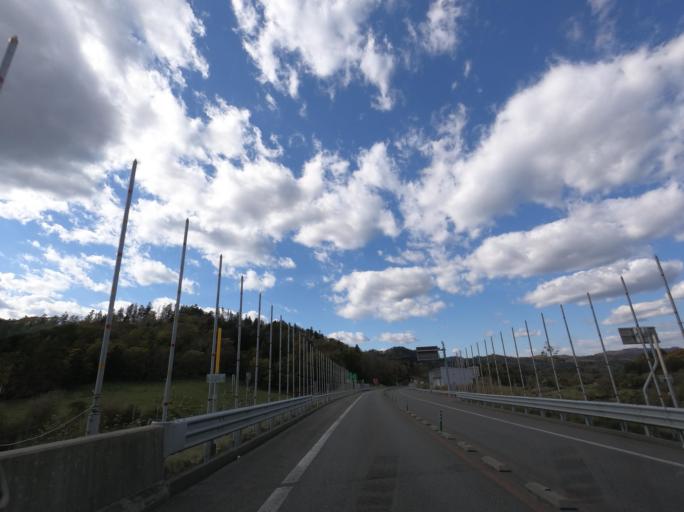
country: JP
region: Hokkaido
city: Kushiro
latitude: 43.0755
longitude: 144.0736
